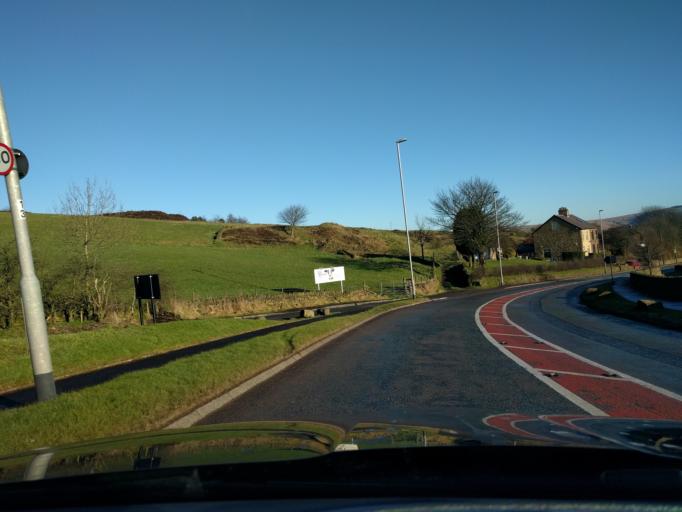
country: GB
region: England
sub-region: Borough of Oldham
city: Delph
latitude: 53.5521
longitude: -2.0380
